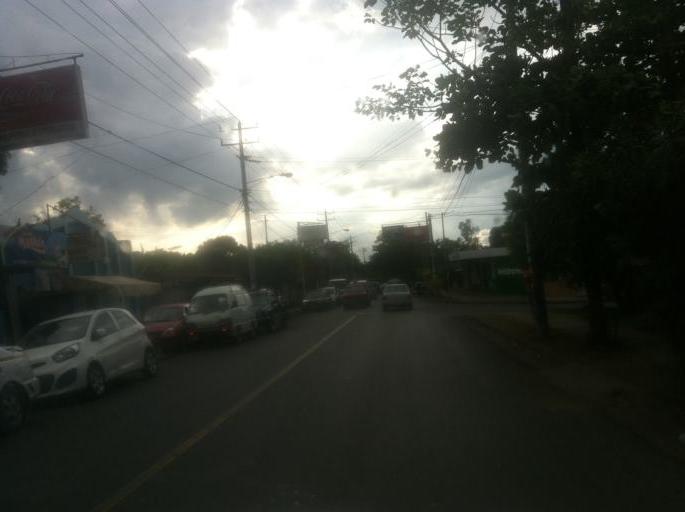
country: NI
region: Managua
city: Managua
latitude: 12.1193
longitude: -86.2406
